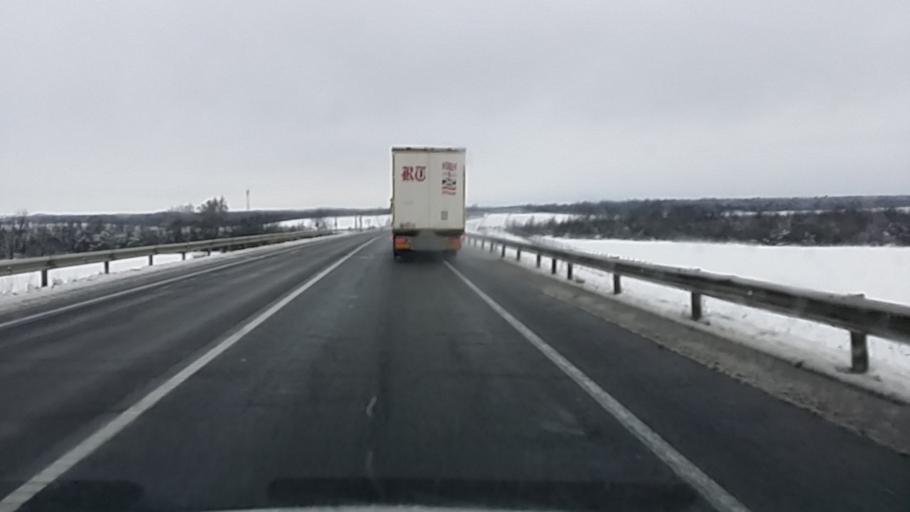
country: HU
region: Gyor-Moson-Sopron
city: Rajka
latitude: 47.9365
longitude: 17.1677
